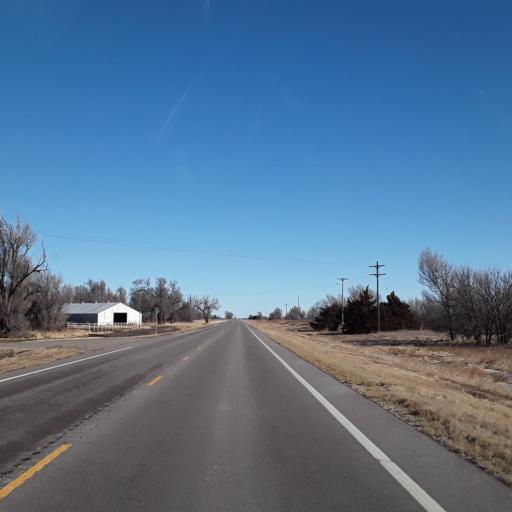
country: US
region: Kansas
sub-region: Pawnee County
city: Larned
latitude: 38.1158
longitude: -99.1853
